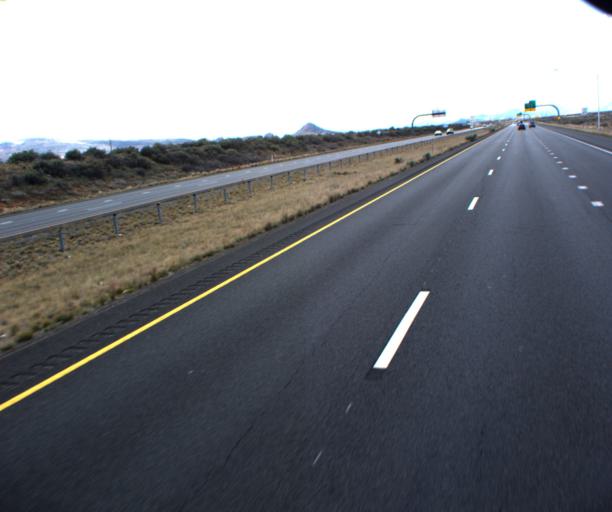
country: US
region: Arizona
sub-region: Yavapai County
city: Prescott Valley
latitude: 34.6348
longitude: -112.3421
